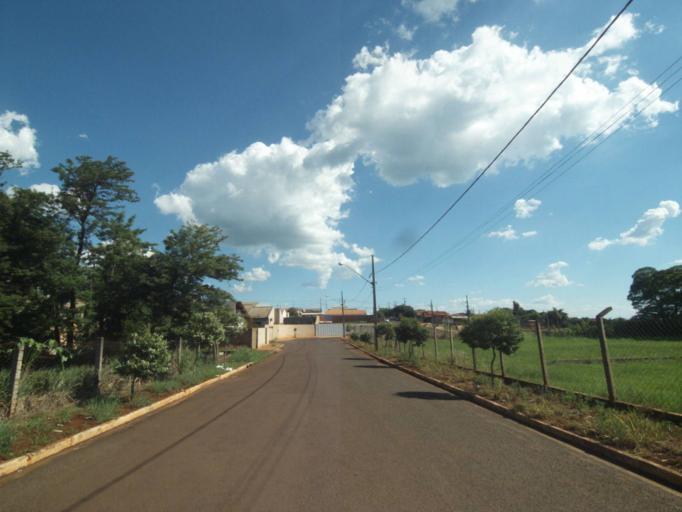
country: BR
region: Parana
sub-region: Sertanopolis
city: Sertanopolis
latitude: -23.0437
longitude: -50.8182
